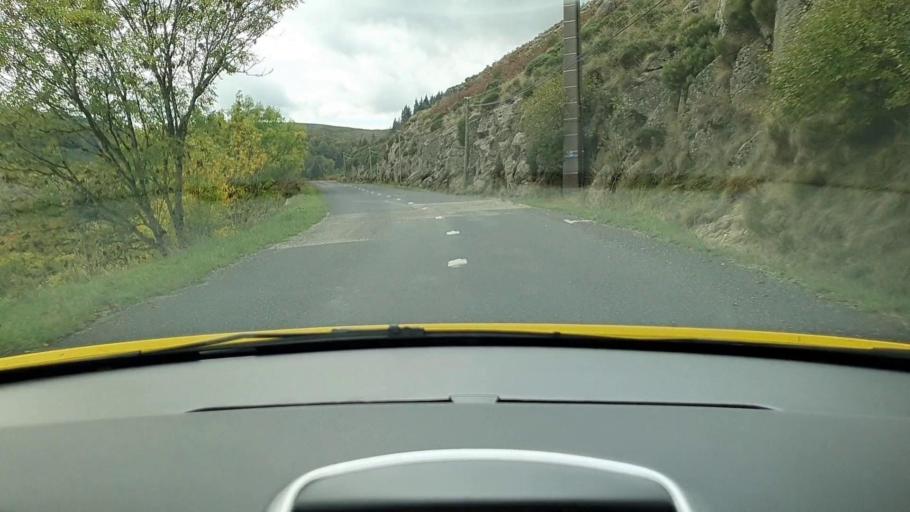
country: FR
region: Languedoc-Roussillon
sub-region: Departement de la Lozere
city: Meyrueis
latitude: 44.0766
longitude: 3.4834
